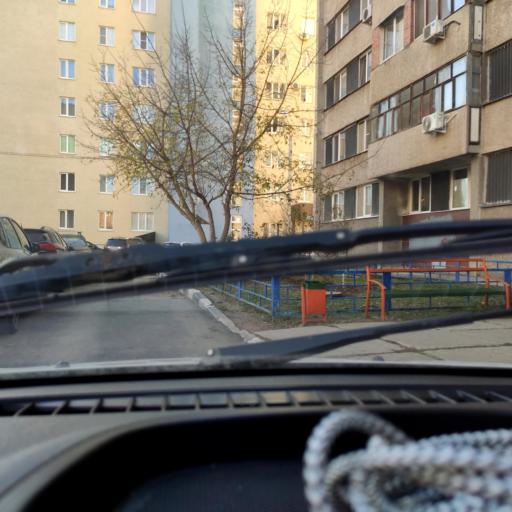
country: RU
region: Samara
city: Zhigulevsk
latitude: 53.4731
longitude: 49.4718
